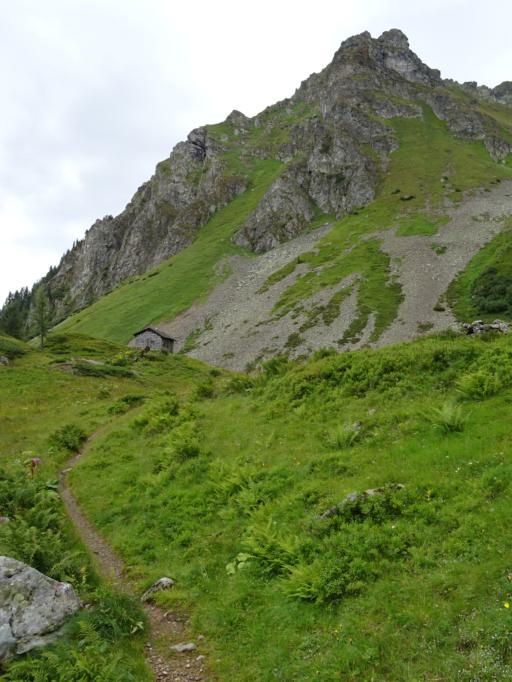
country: AT
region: Salzburg
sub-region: Politischer Bezirk Sankt Johann im Pongau
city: Untertauern
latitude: 47.2759
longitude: 13.5681
